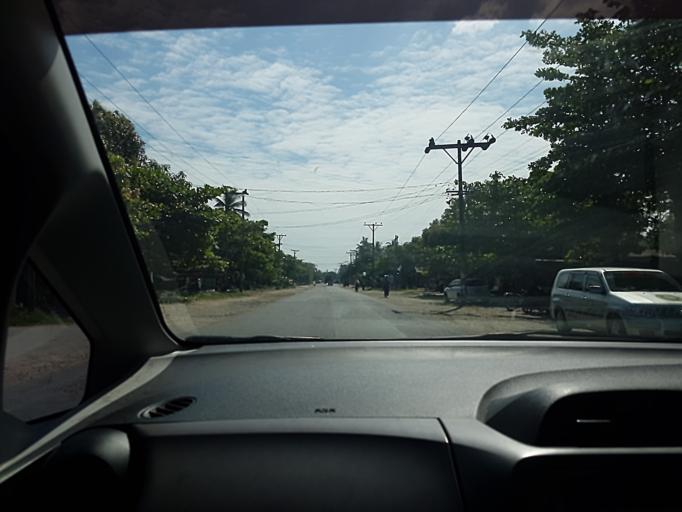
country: MM
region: Mon
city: Thaton
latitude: 16.6949
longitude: 97.4256
